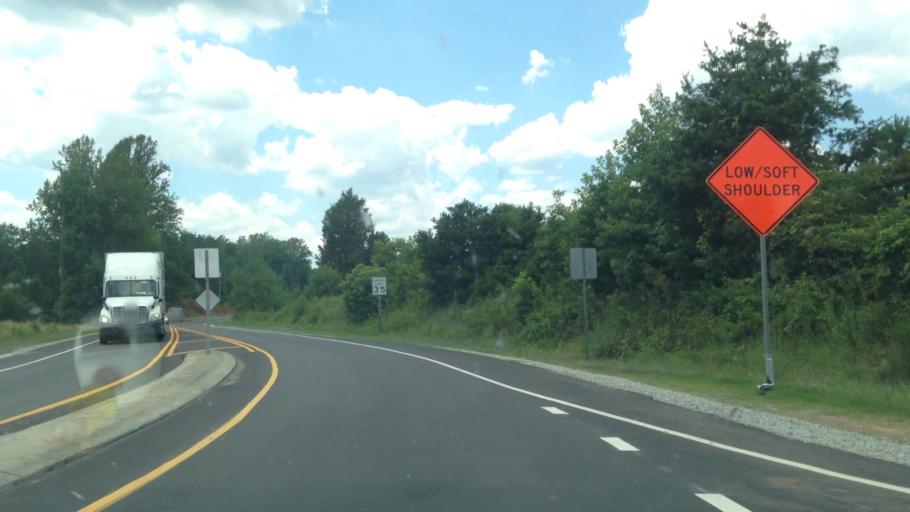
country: US
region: North Carolina
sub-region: Guilford County
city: Stokesdale
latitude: 36.2457
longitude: -79.9735
